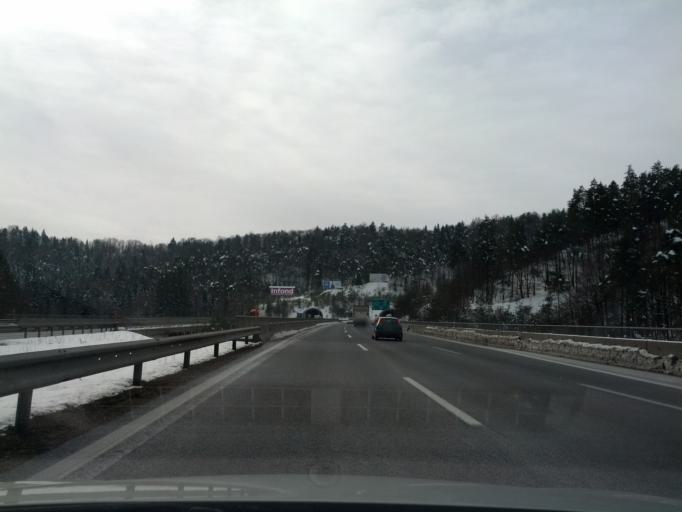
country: SI
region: Skofljica
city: Lavrica
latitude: 46.0249
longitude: 14.5660
